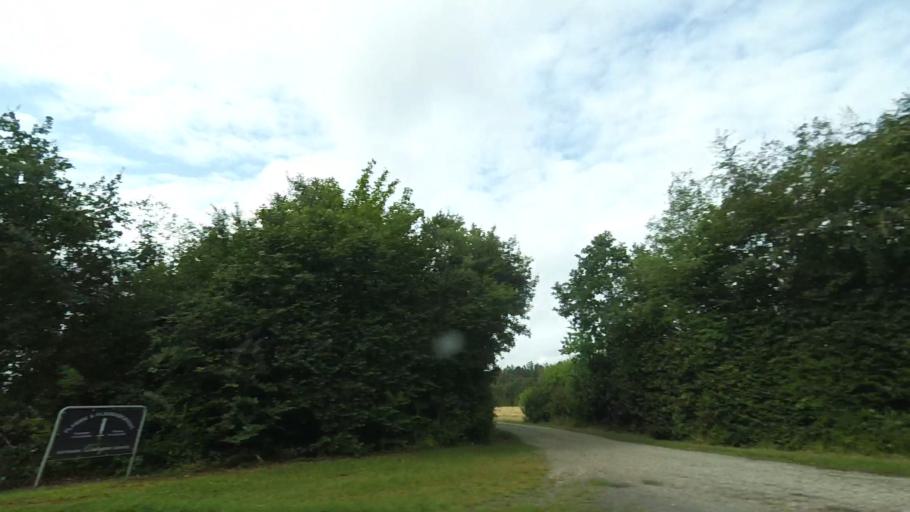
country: DK
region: Central Jutland
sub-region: Syddjurs Kommune
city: Ryomgard
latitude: 56.3634
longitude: 10.5100
